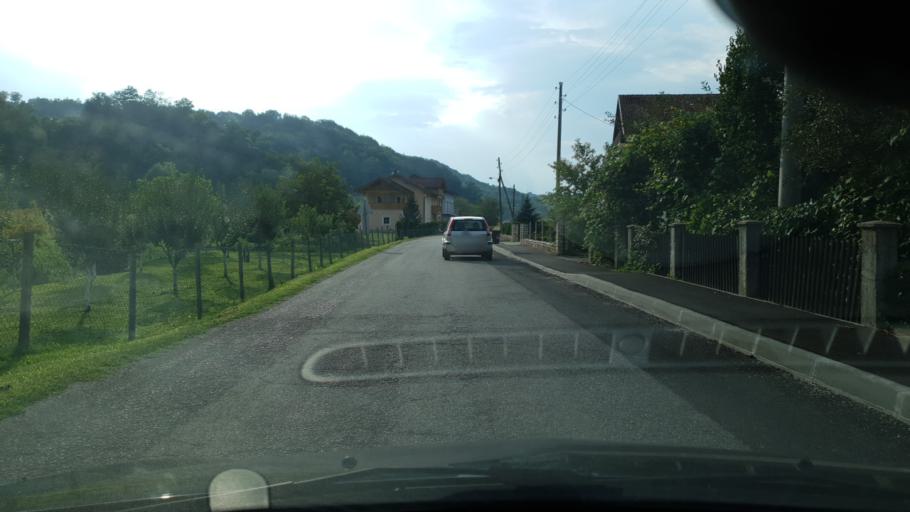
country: HR
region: Krapinsko-Zagorska
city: Zabok
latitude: 46.0790
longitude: 15.8997
